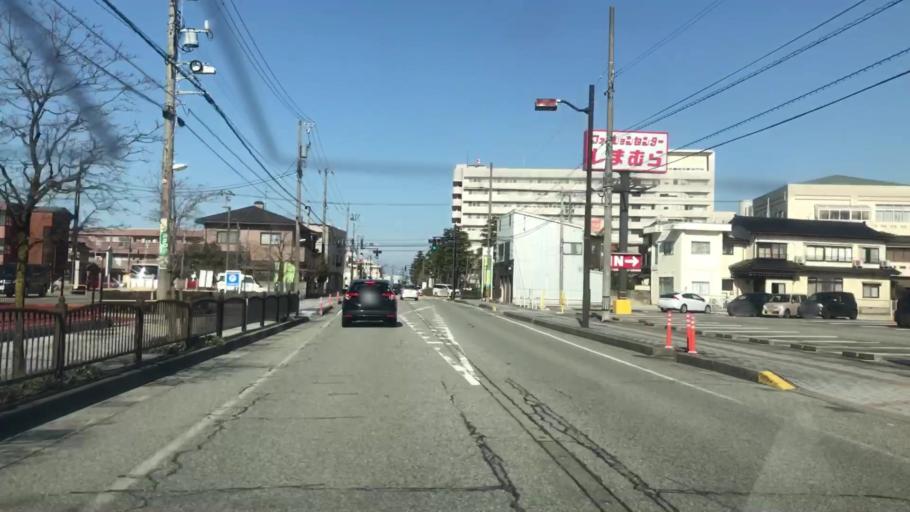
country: JP
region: Toyama
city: Toyama-shi
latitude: 36.6904
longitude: 137.2364
